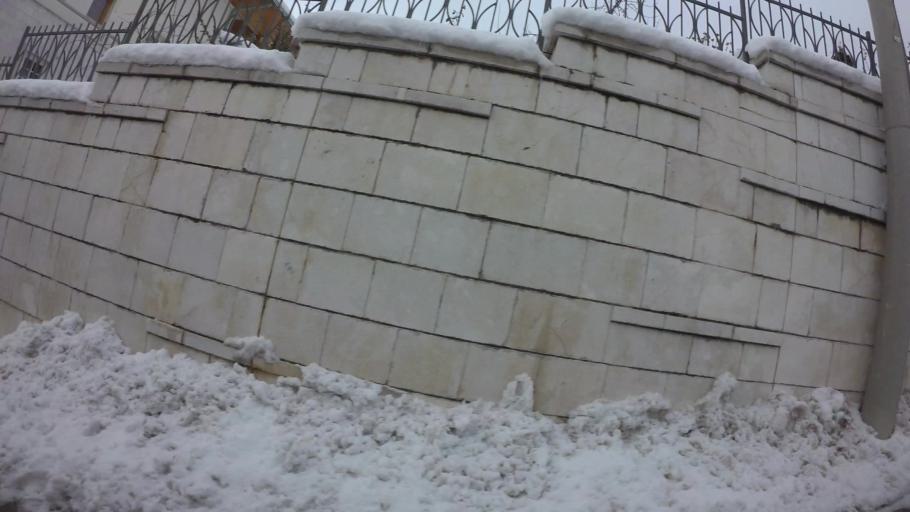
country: BA
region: Federation of Bosnia and Herzegovina
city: Kobilja Glava
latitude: 43.8711
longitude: 18.4381
